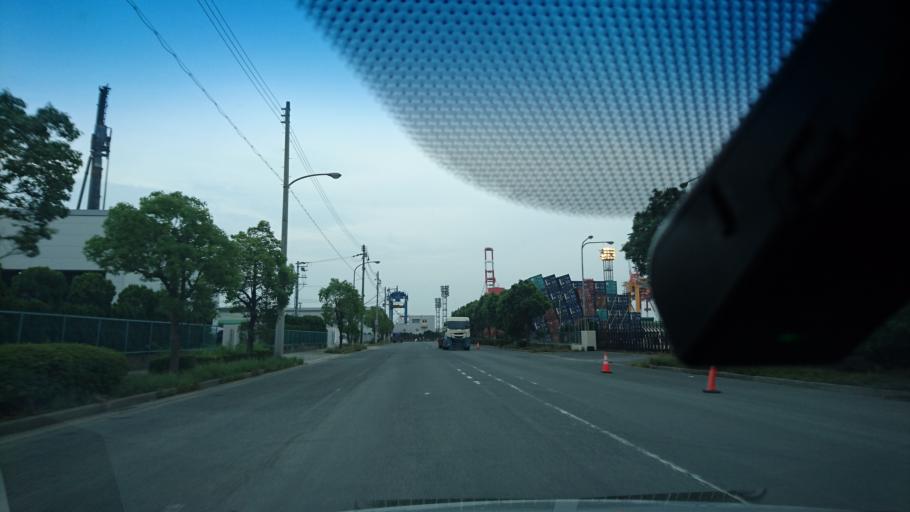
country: JP
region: Hyogo
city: Ashiya
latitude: 34.6834
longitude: 135.2578
